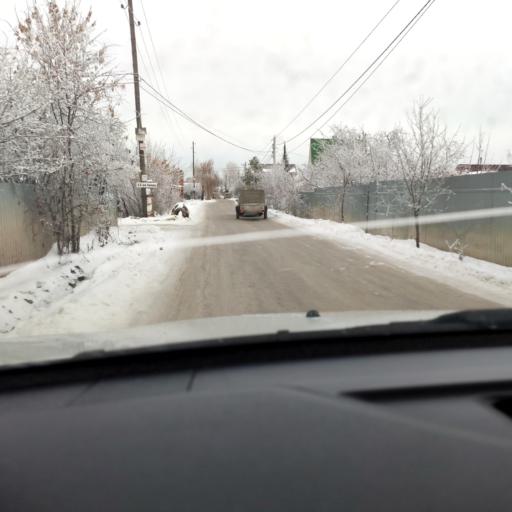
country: RU
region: Samara
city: Petra-Dubrava
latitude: 53.2994
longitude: 50.2503
